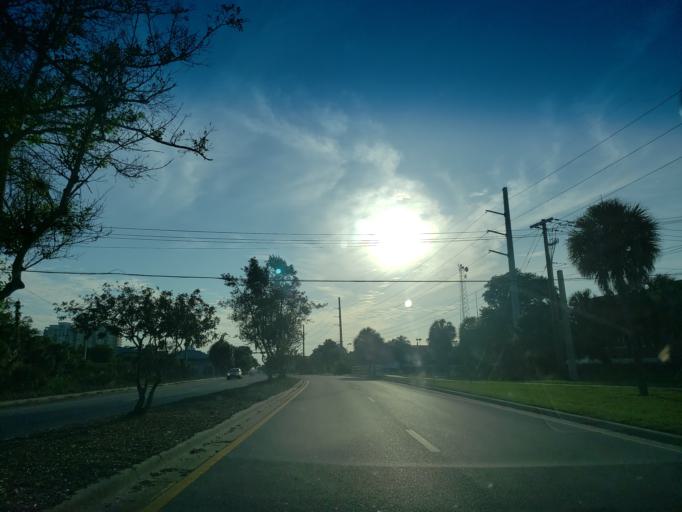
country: US
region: Florida
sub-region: Sarasota County
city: Sarasota
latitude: 27.3447
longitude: -82.5391
